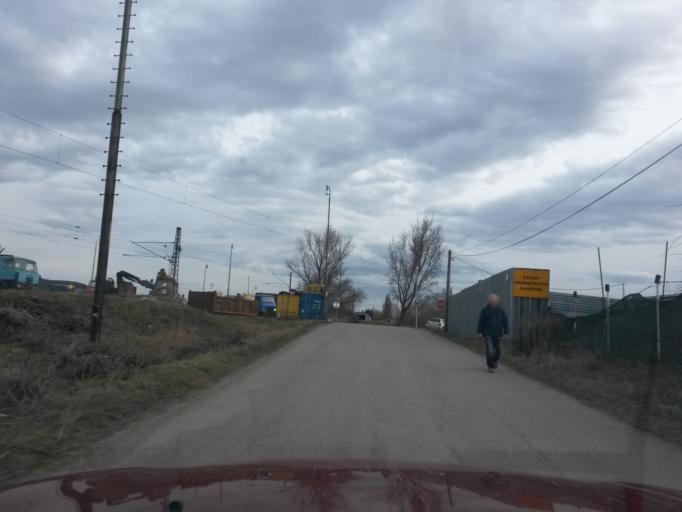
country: SK
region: Kosicky
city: Kosice
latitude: 48.7181
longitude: 21.2710
